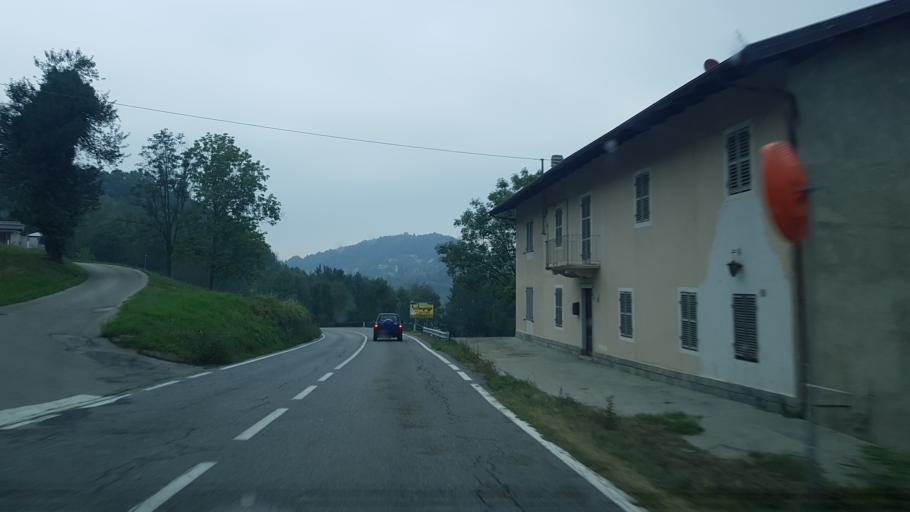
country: IT
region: Piedmont
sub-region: Provincia di Cuneo
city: Frabosa Sottana
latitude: 44.3172
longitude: 7.8035
